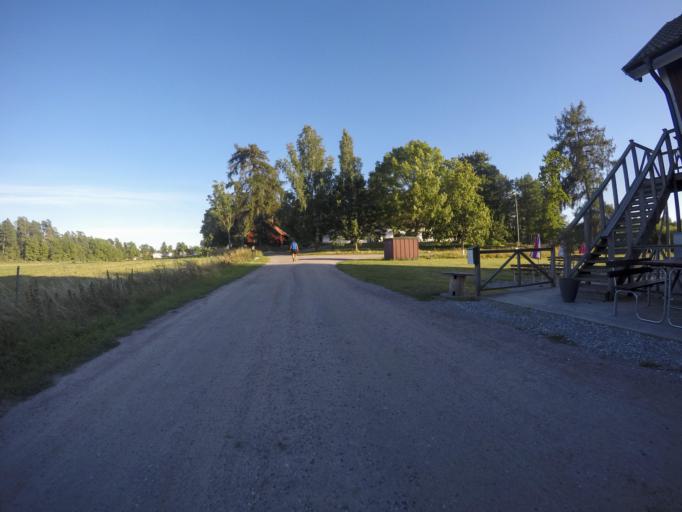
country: SE
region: Vaestmanland
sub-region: Vasteras
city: Vasteras
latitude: 59.5538
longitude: 16.6612
